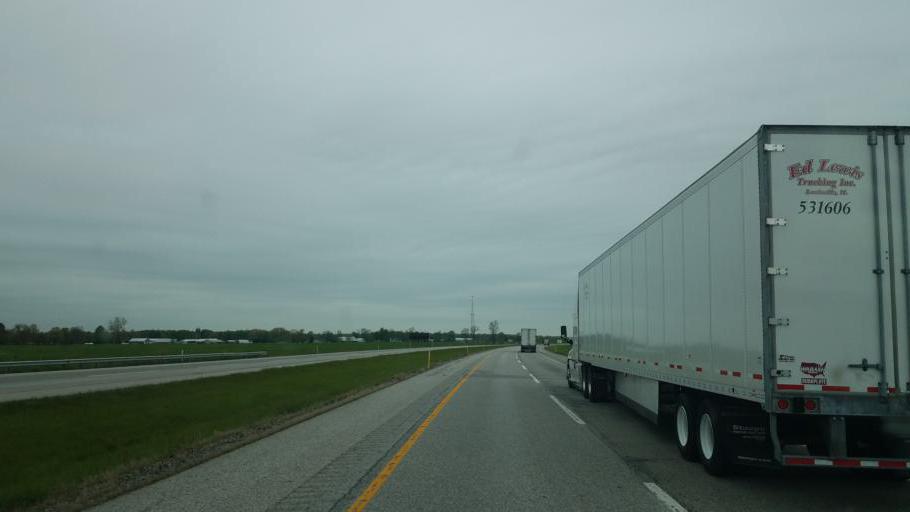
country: US
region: Michigan
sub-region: Saint Joseph County
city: Sturgis
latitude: 41.7475
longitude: -85.5010
